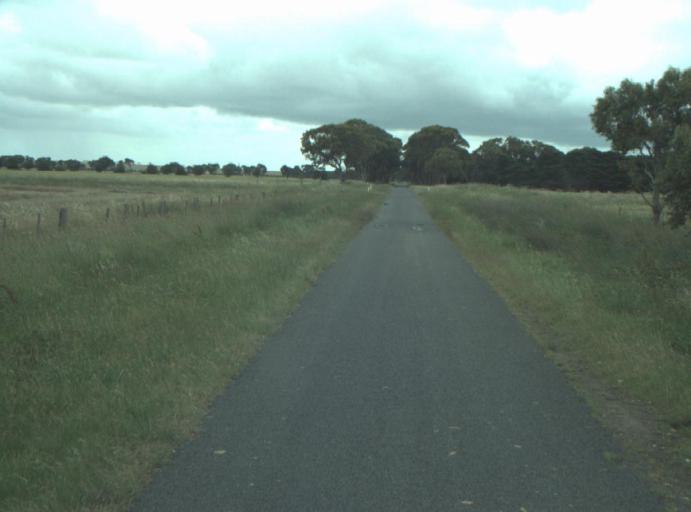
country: AU
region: Victoria
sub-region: Greater Geelong
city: Lara
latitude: -37.8612
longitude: 144.3517
